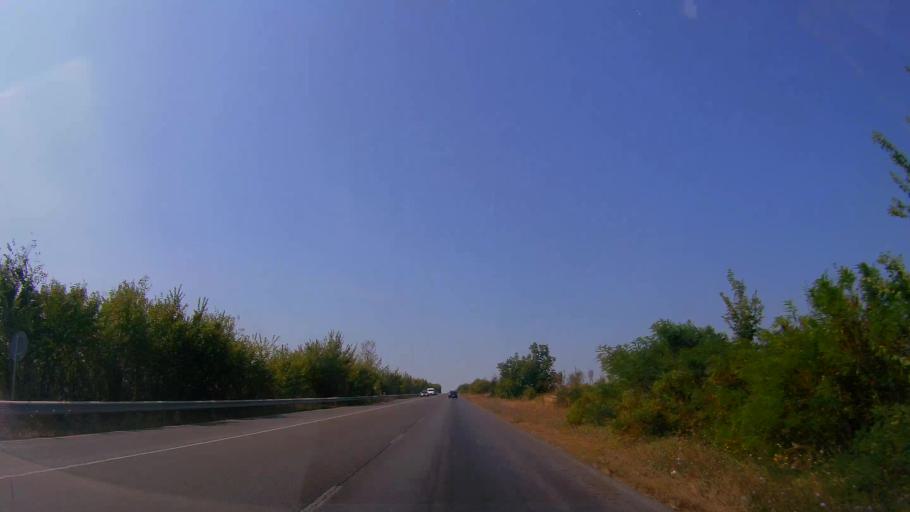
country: BG
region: Ruse
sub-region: Obshtina Vetovo
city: Senovo
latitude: 43.5612
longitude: 26.3680
